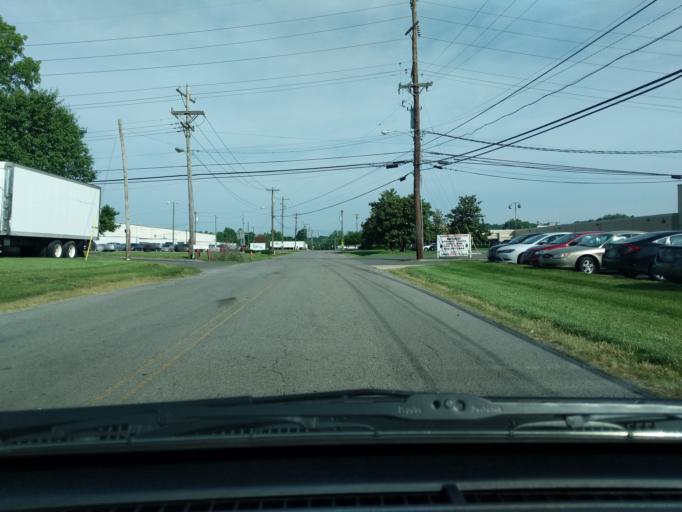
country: US
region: Tennessee
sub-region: Davidson County
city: Oak Hill
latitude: 36.0913
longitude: -86.6908
